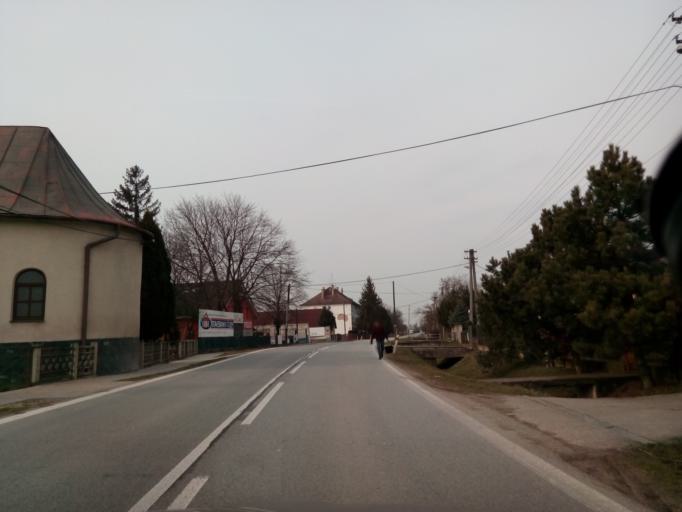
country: HU
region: Borsod-Abauj-Zemplen
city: Satoraljaujhely
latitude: 48.4633
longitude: 21.6401
